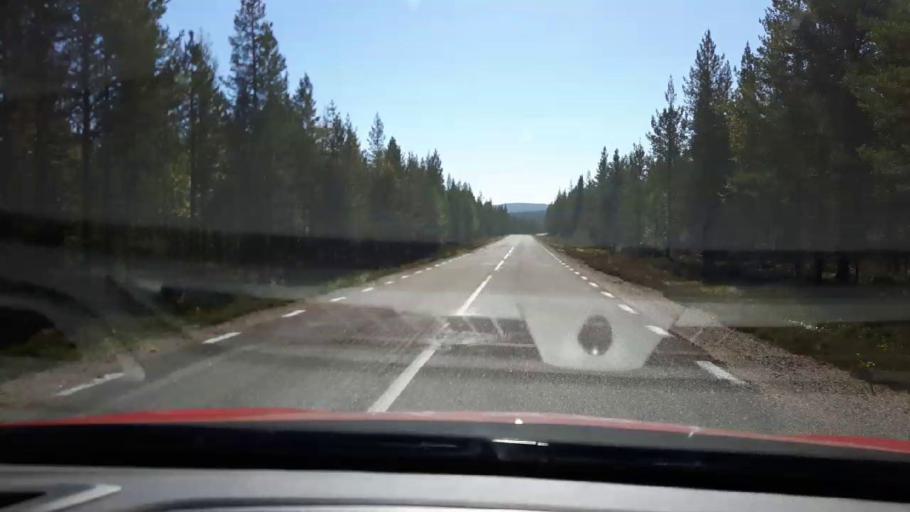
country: SE
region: Jaemtland
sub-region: Harjedalens Kommun
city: Sveg
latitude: 61.7230
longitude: 14.1672
